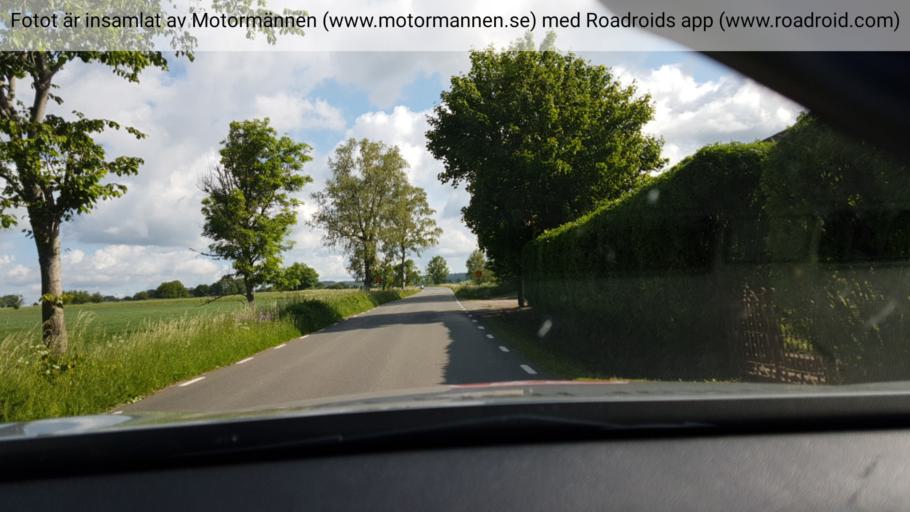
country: SE
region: Vaestra Goetaland
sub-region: Falkopings Kommun
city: Akarp
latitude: 58.3086
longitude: 13.6098
